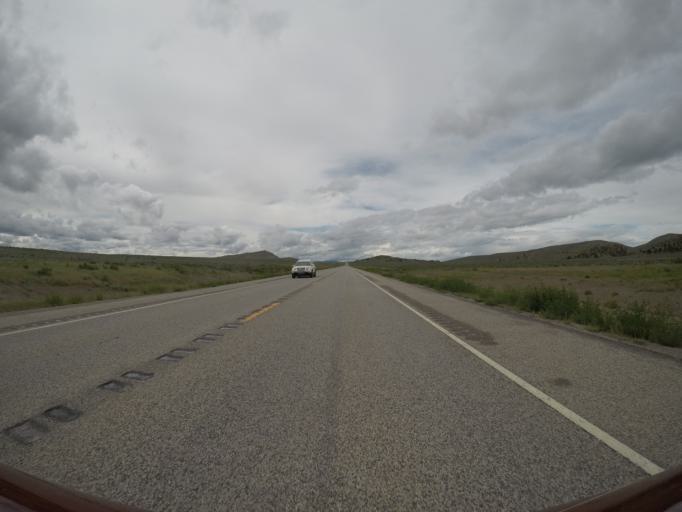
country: US
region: Montana
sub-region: Carbon County
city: Red Lodge
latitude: 45.1998
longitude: -108.8616
